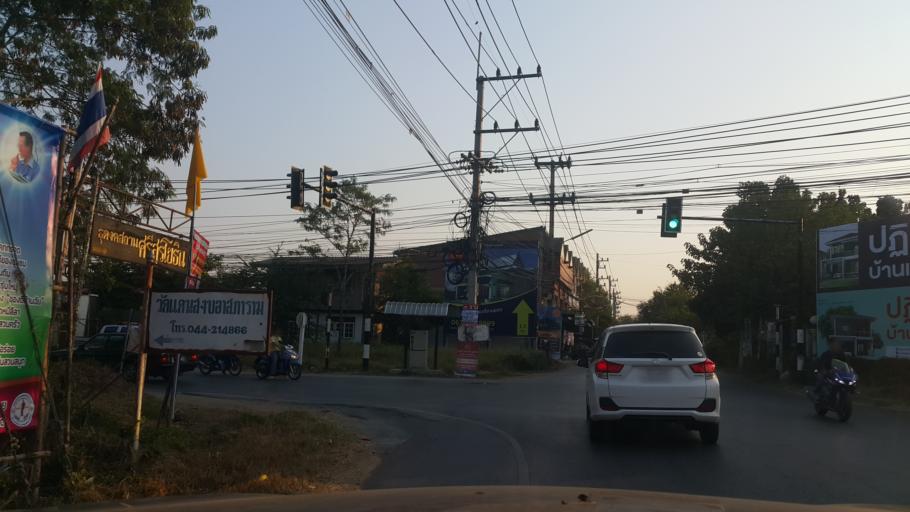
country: TH
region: Nakhon Ratchasima
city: Nakhon Ratchasima
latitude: 14.9382
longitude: 102.0280
